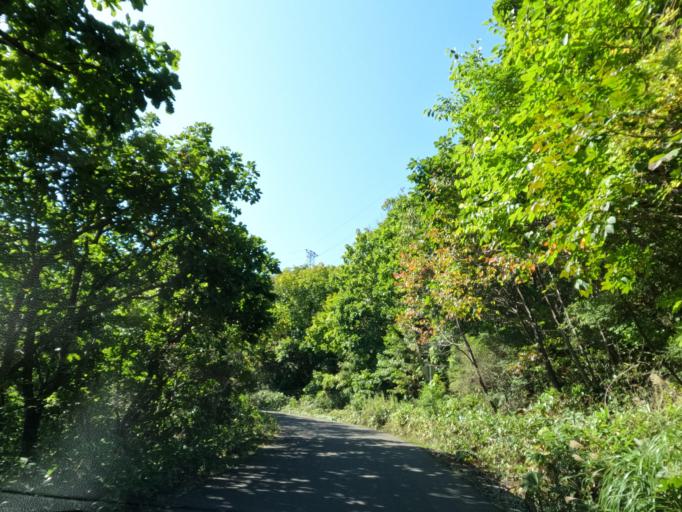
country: JP
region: Hokkaido
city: Muroran
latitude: 42.3662
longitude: 141.0200
